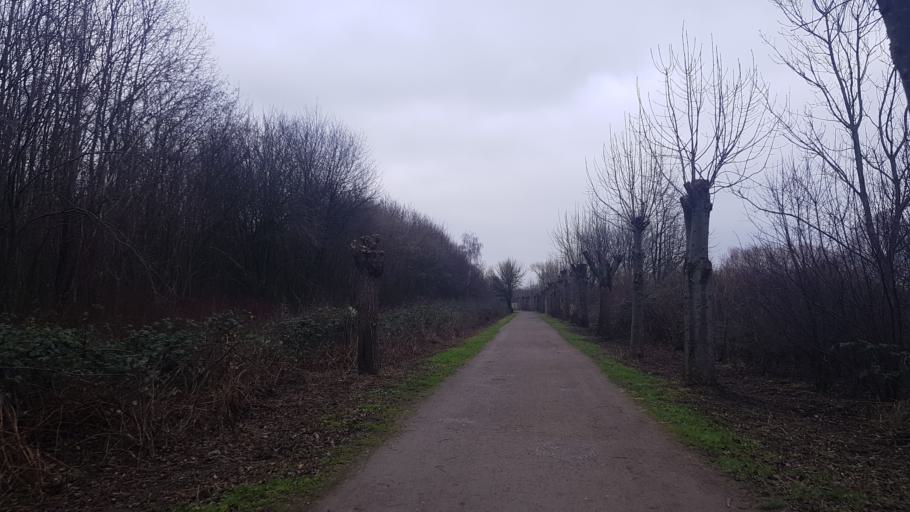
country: DE
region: North Rhine-Westphalia
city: Meiderich
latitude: 51.4543
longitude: 6.8072
